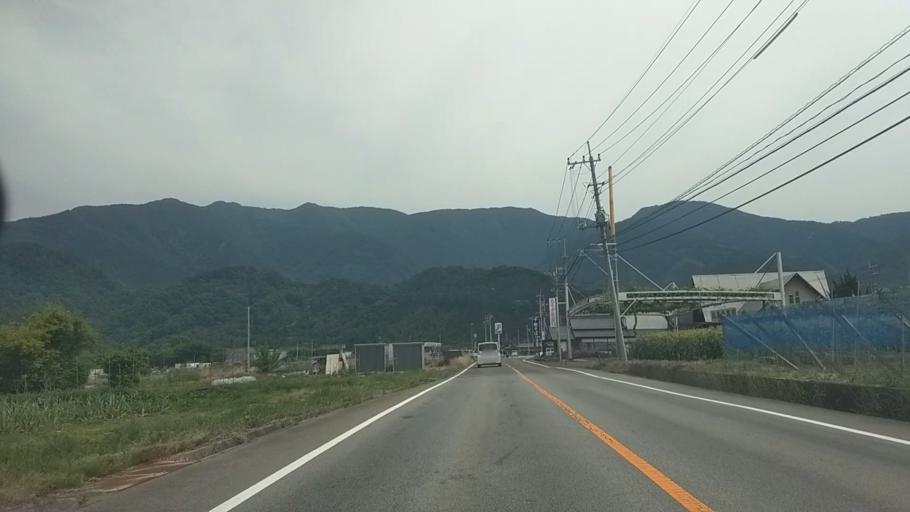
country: JP
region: Yamanashi
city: Isawa
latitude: 35.5831
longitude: 138.5906
